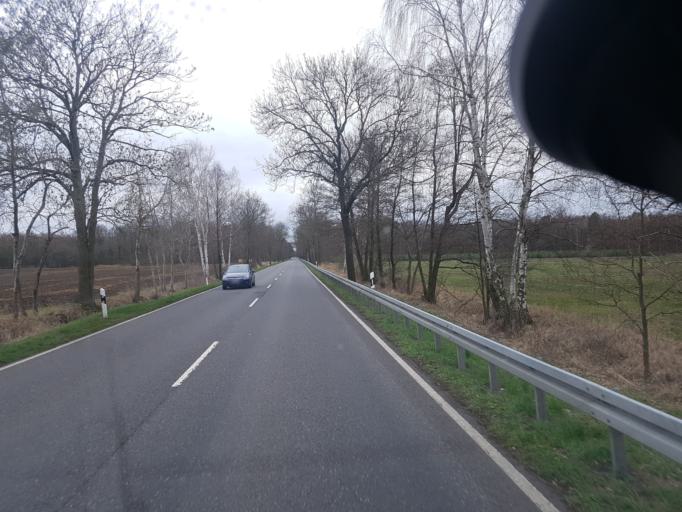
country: DE
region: Brandenburg
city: Luebben
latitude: 51.9747
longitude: 13.9565
